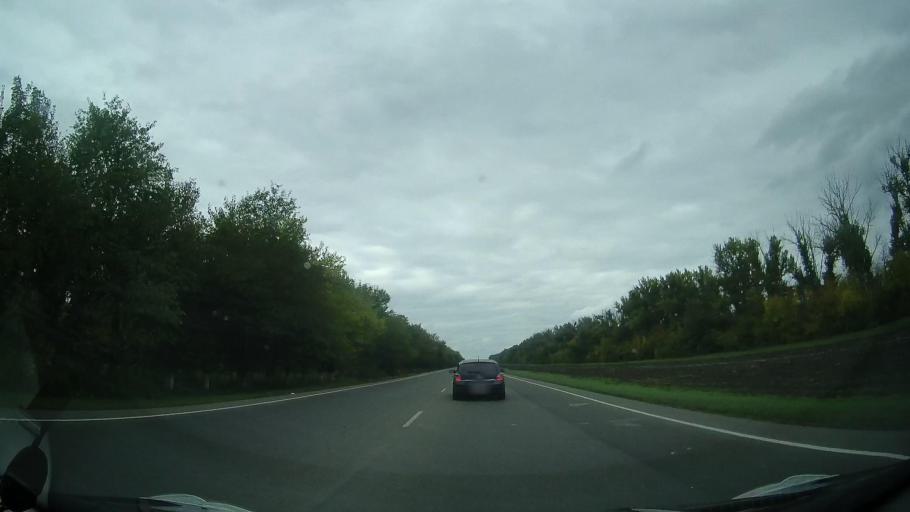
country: RU
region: Rostov
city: Yegorlykskaya
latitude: 46.6065
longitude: 40.6121
